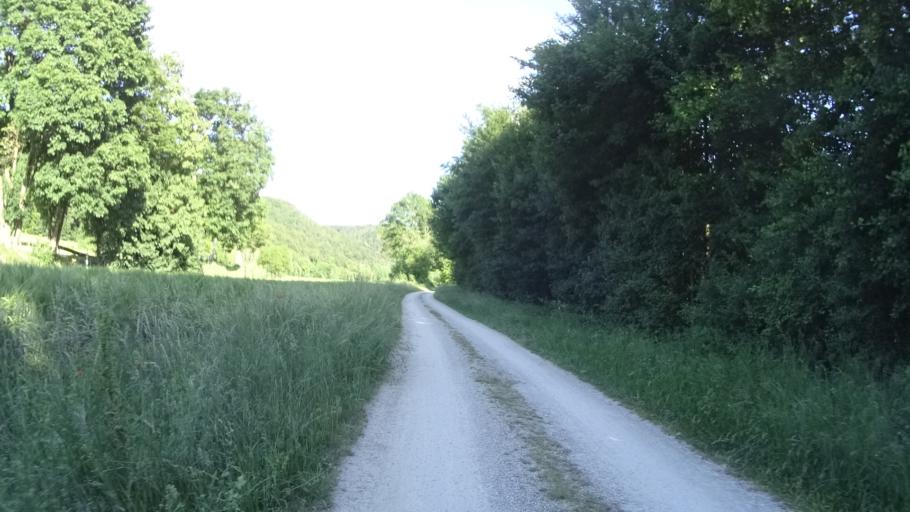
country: DE
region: Bavaria
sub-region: Upper Palatinate
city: Dietfurt
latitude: 49.0093
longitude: 11.6197
